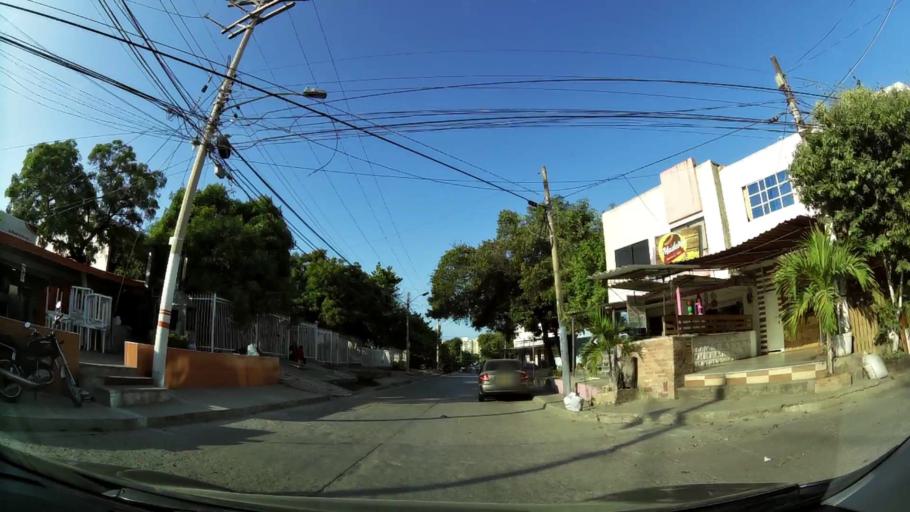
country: CO
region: Bolivar
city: Cartagena
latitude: 10.3826
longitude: -75.4797
